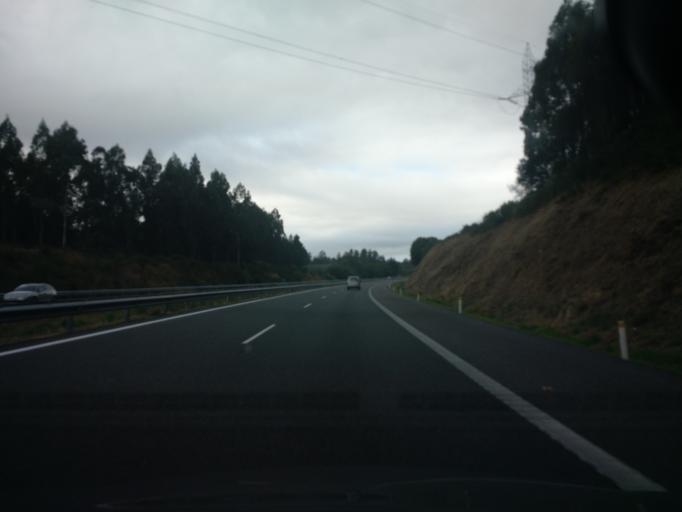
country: ES
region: Galicia
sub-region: Provincia da Coruna
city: Abegondo
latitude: 43.2177
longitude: -8.2756
